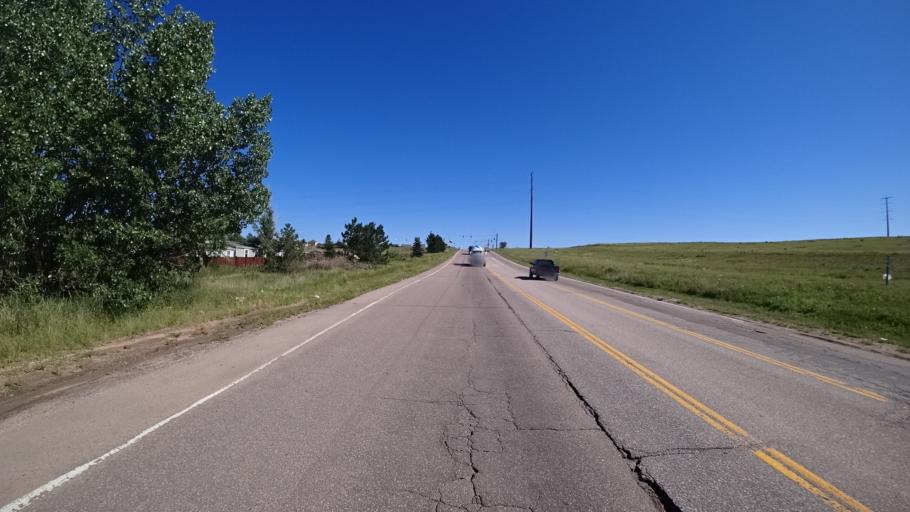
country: US
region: Colorado
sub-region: El Paso County
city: Cimarron Hills
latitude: 38.8991
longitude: -104.6829
